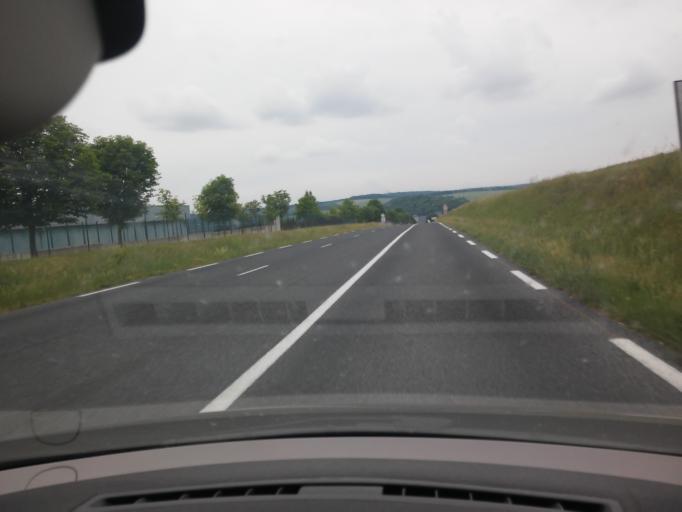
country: FR
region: Lorraine
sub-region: Departement de la Meuse
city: Saint-Mihiel
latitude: 48.8803
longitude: 5.5299
